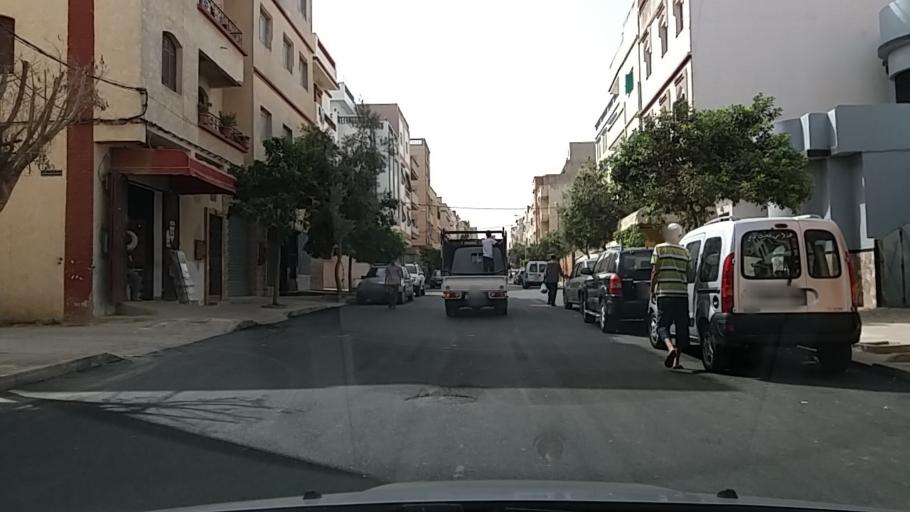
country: MA
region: Tanger-Tetouan
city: Asilah
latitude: 35.4589
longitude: -6.0383
